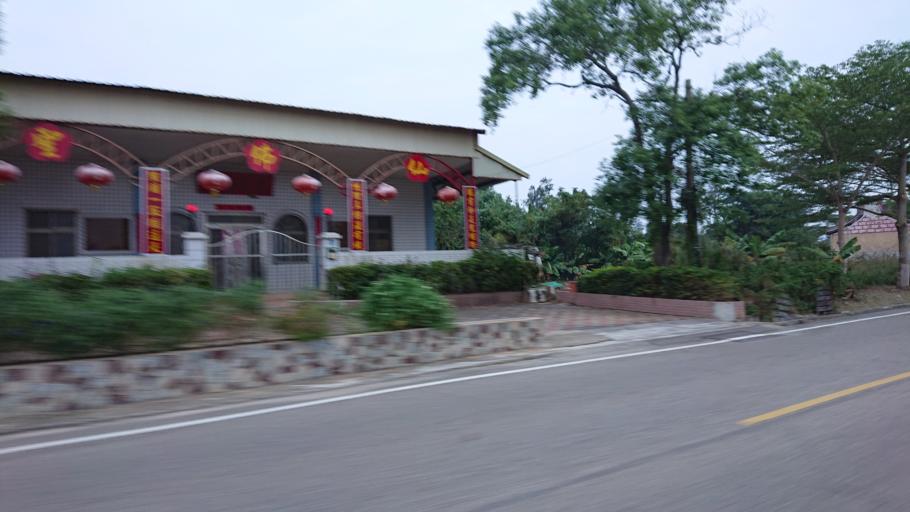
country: TW
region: Fukien
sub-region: Kinmen
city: Jincheng
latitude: 24.4264
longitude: 118.2501
